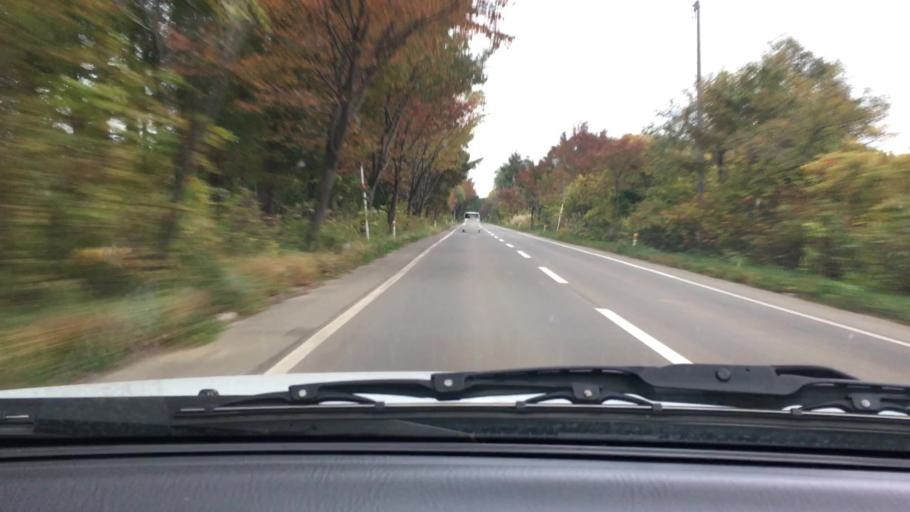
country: JP
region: Aomori
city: Shimokizukuri
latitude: 40.7151
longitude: 140.2955
